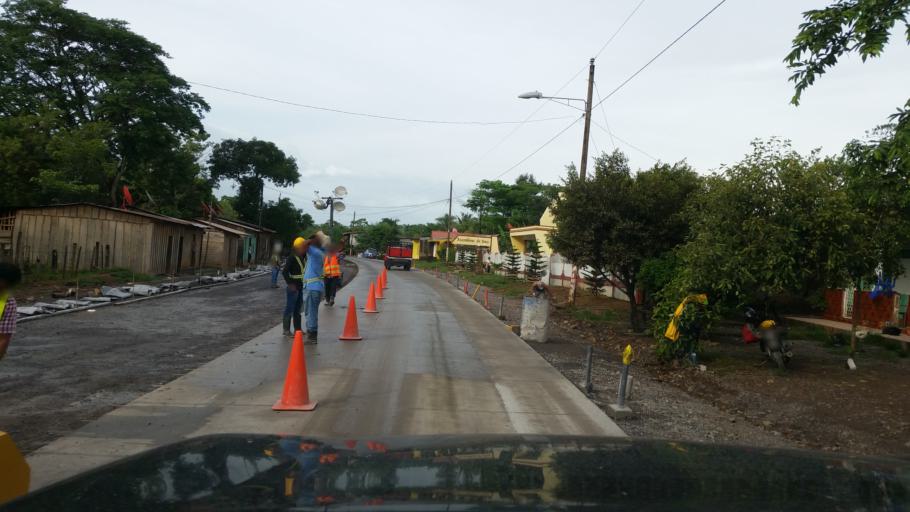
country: NI
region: Matagalpa
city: Rio Blanco
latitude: 13.0724
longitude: -85.0637
